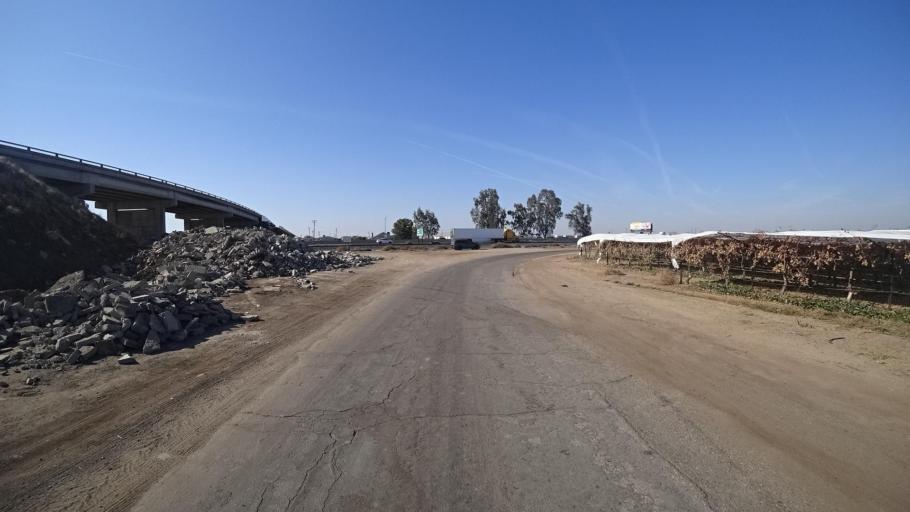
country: US
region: California
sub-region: Kern County
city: McFarland
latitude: 35.6896
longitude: -119.2287
